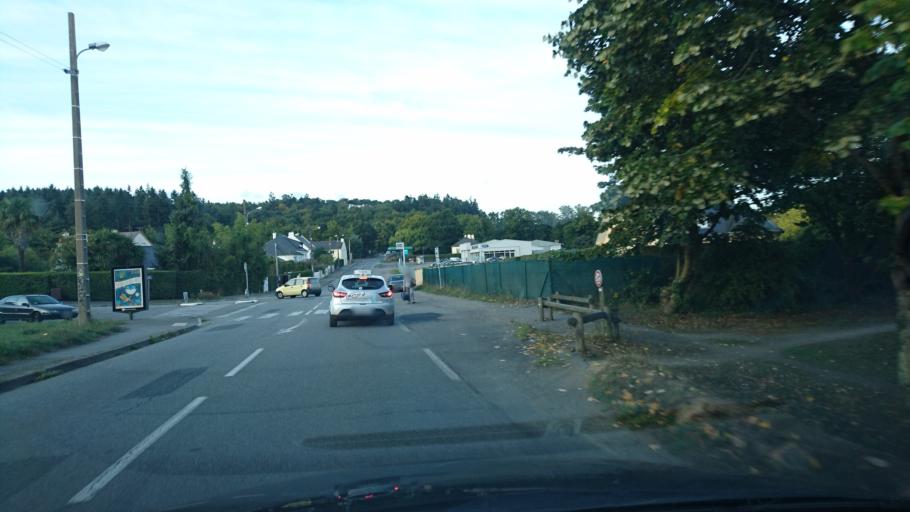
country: FR
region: Brittany
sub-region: Departement d'Ille-et-Vilaine
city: Redon
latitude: 47.6595
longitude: -2.0848
